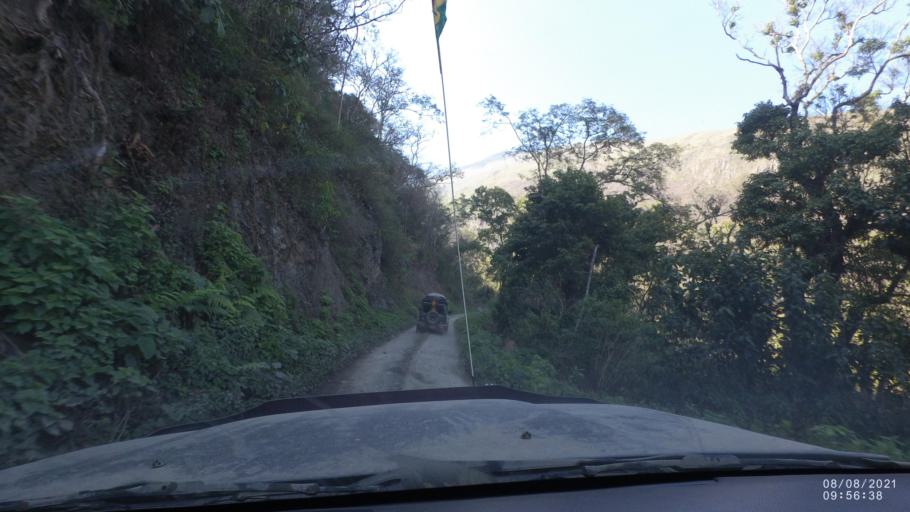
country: BO
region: La Paz
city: Quime
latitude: -16.6383
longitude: -66.7257
